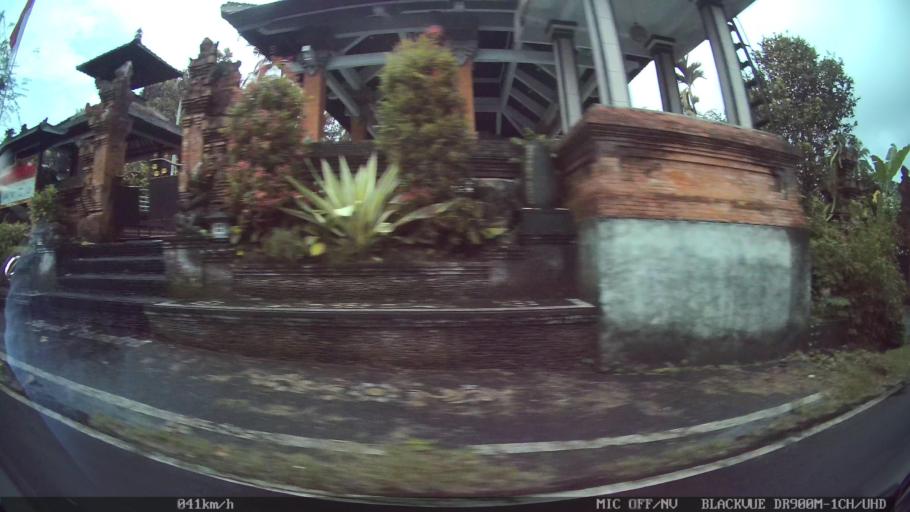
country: ID
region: Bali
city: Pegongan
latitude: -8.4934
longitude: 115.2370
